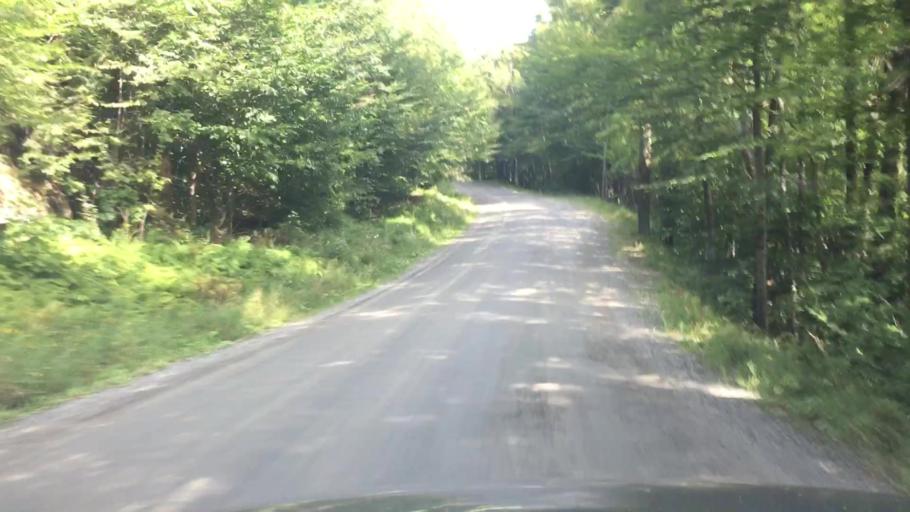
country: US
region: Vermont
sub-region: Windham County
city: Dover
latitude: 42.8389
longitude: -72.8205
